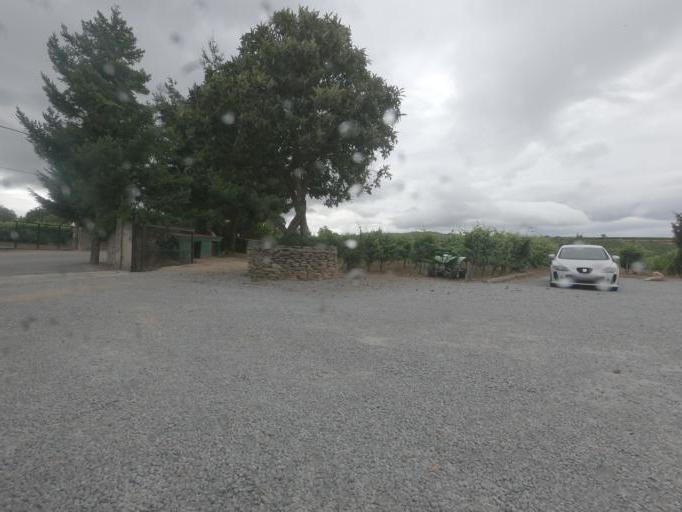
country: PT
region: Vila Real
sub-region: Sabrosa
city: Sabrosa
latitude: 41.2502
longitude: -7.4963
